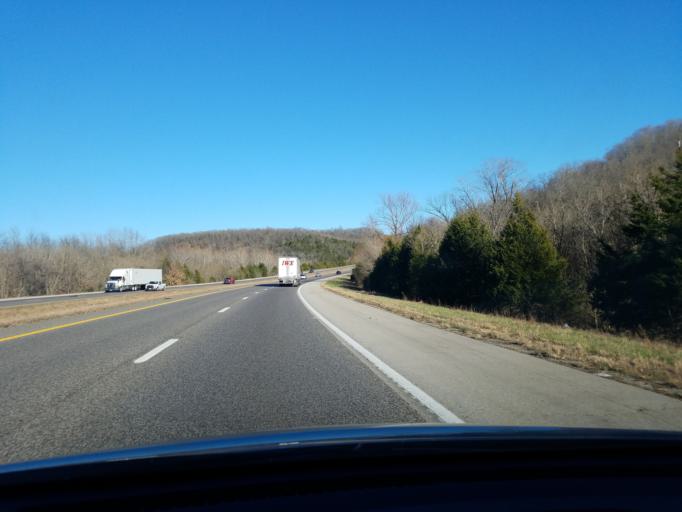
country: US
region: Missouri
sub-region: Pulaski County
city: Saint Robert
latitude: 37.8609
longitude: -92.0682
